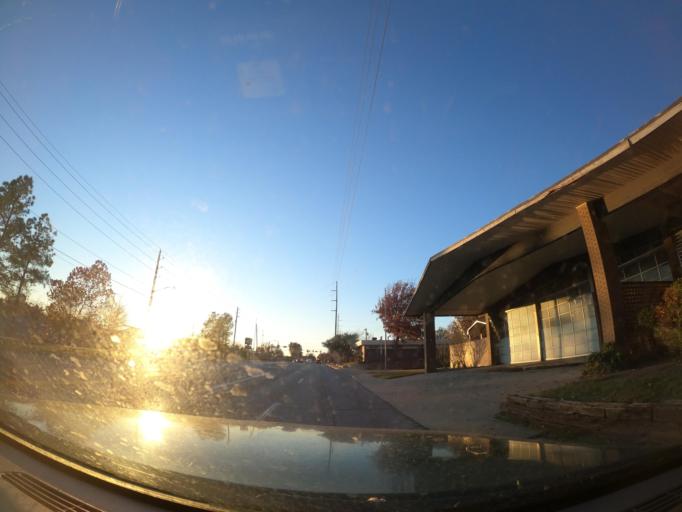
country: US
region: Oklahoma
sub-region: Tulsa County
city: Tulsa
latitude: 36.1407
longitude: -95.9212
